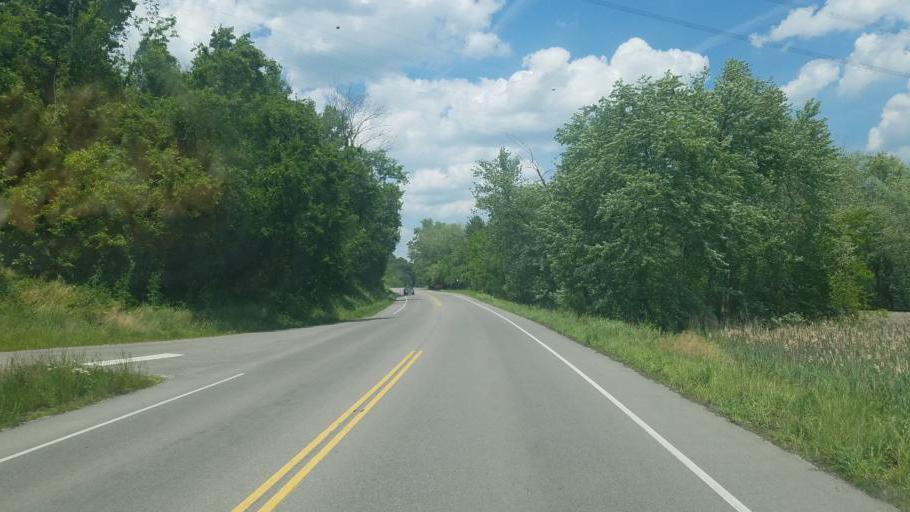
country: US
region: Ohio
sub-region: Meigs County
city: Middleport
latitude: 38.9661
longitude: -82.0964
